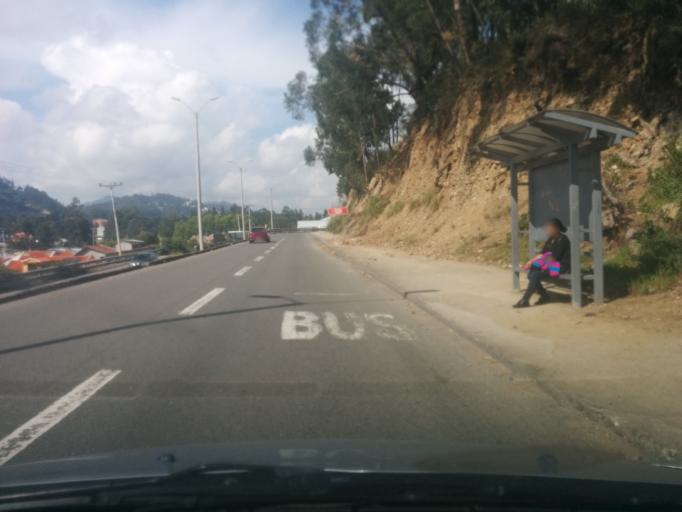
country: EC
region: Azuay
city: Cuenca
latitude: -2.8890
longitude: -78.9615
